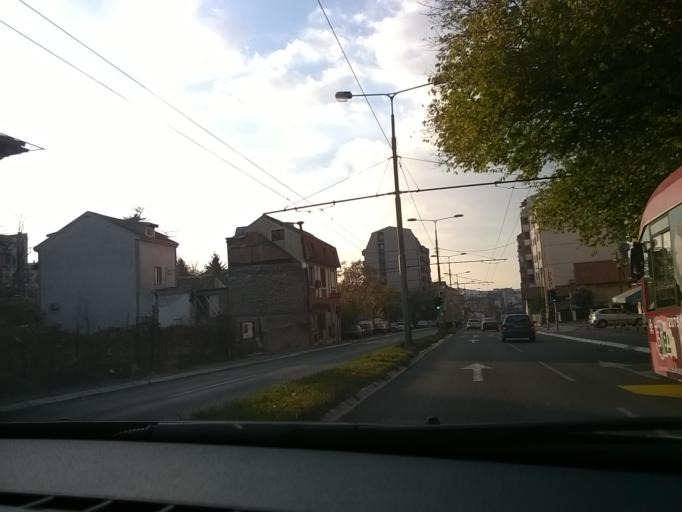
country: RS
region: Central Serbia
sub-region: Belgrade
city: Vracar
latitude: 44.8007
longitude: 20.4958
